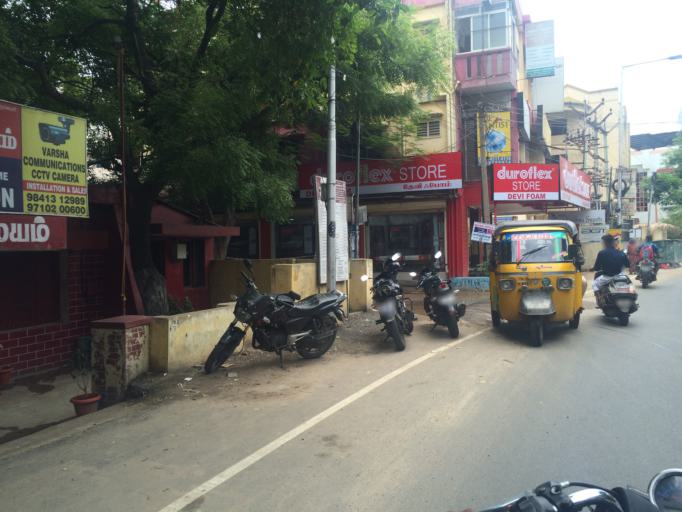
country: IN
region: Tamil Nadu
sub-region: Kancheepuram
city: Alandur
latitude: 12.9809
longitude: 80.2210
